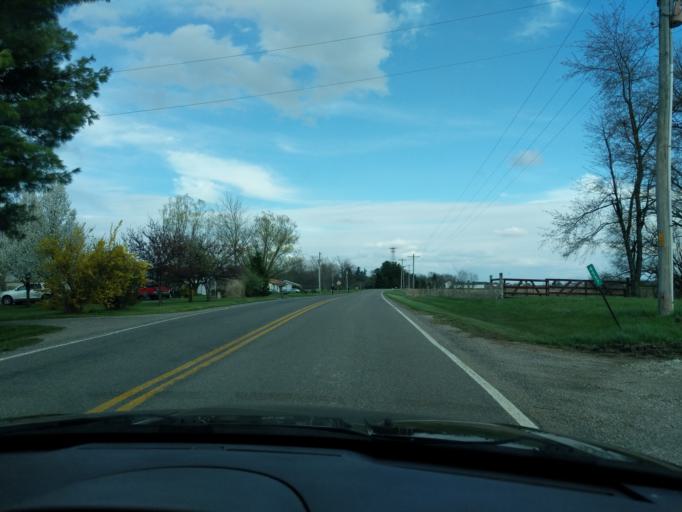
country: US
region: Ohio
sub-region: Champaign County
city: Urbana
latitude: 40.1554
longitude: -83.6574
